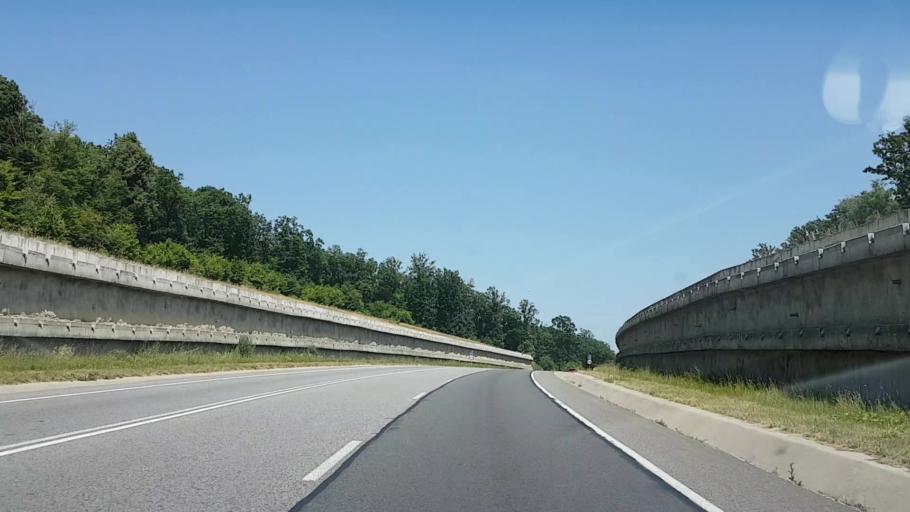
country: RO
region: Cluj
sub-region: Comuna Feleacu
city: Feleacu
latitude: 46.7100
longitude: 23.6475
